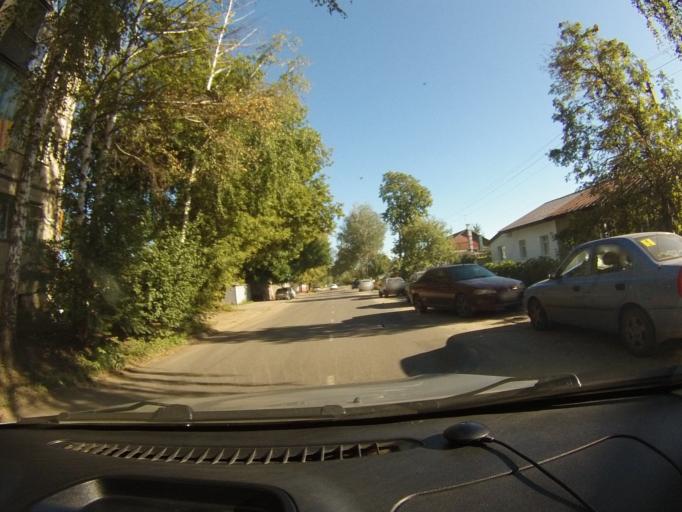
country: RU
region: Tambov
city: Tambov
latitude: 52.7590
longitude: 41.4212
